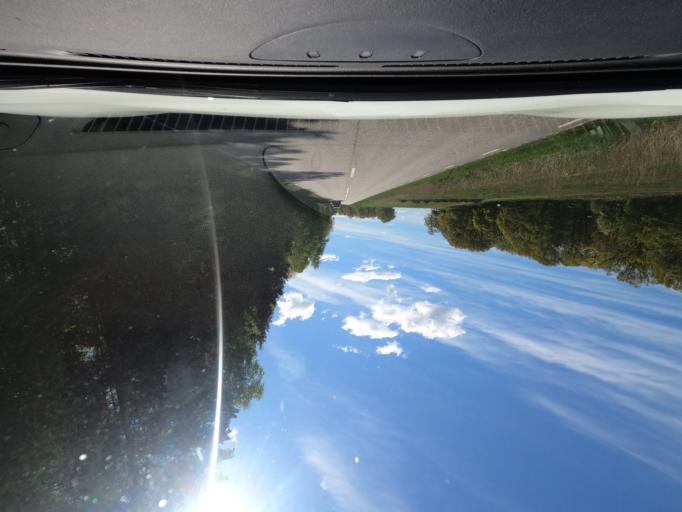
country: SE
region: Halland
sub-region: Kungsbacka Kommun
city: Fjaeras kyrkby
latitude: 57.4365
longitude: 12.1767
